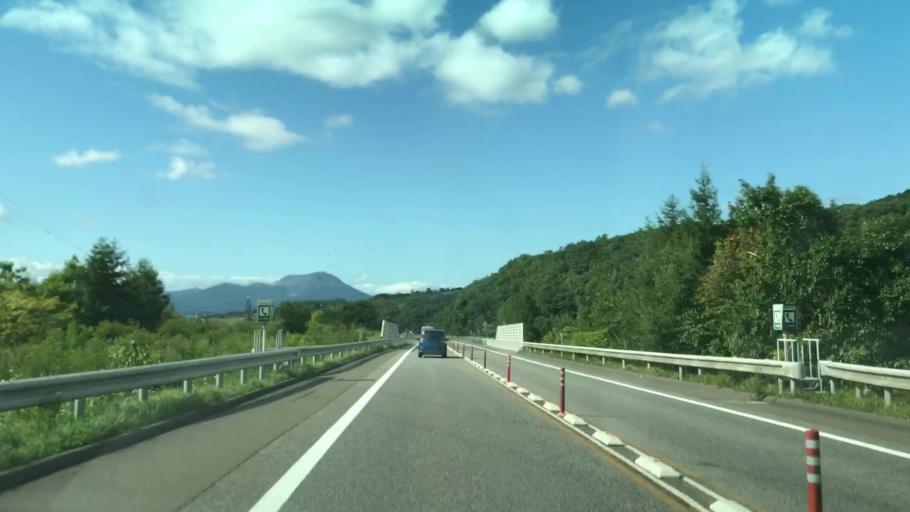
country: JP
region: Hokkaido
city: Date
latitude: 42.4271
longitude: 140.9271
